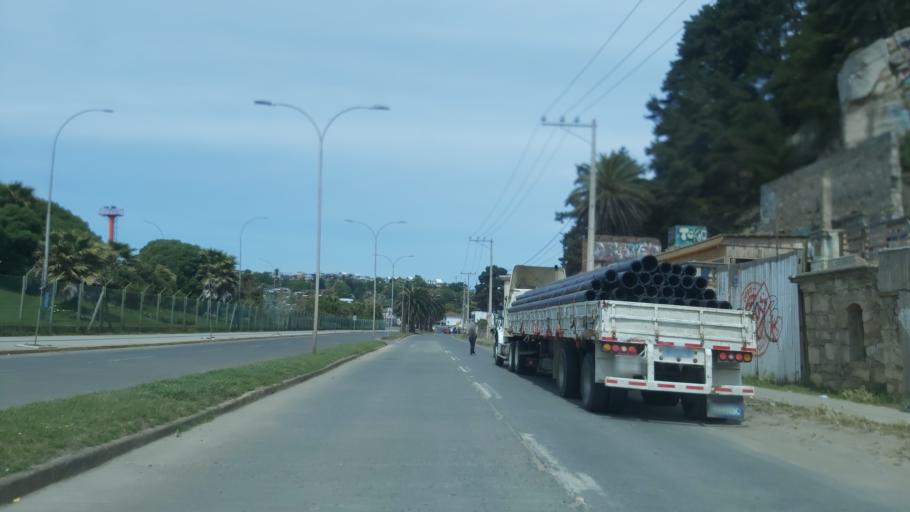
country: CL
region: Maule
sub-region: Provincia de Talca
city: Constitucion
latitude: -35.3263
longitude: -72.4237
